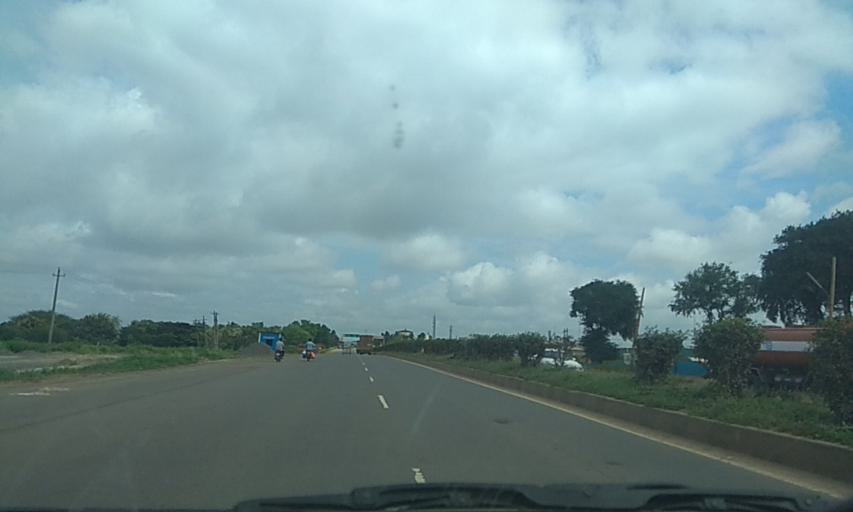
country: IN
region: Karnataka
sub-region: Dharwad
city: Hubli
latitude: 15.3099
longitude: 75.1455
